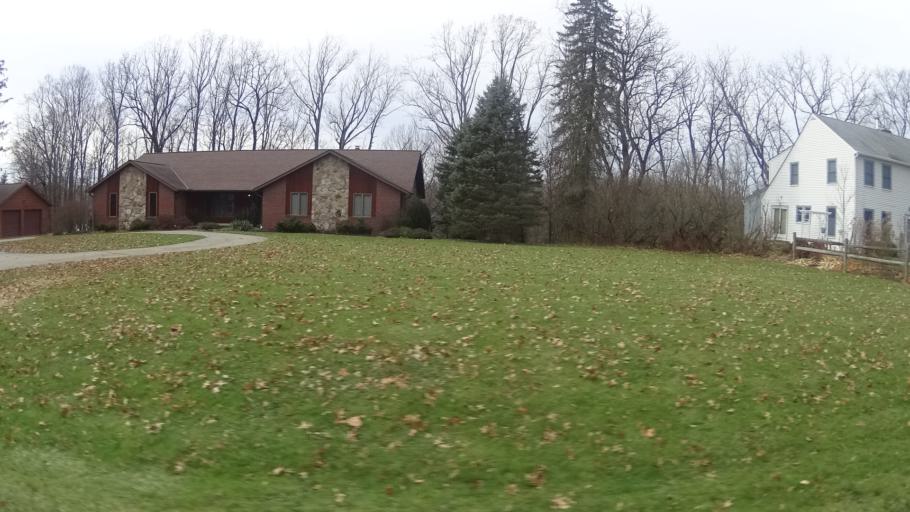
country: US
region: Ohio
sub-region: Cuyahoga County
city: Strongsville
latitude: 41.2913
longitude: -81.9116
